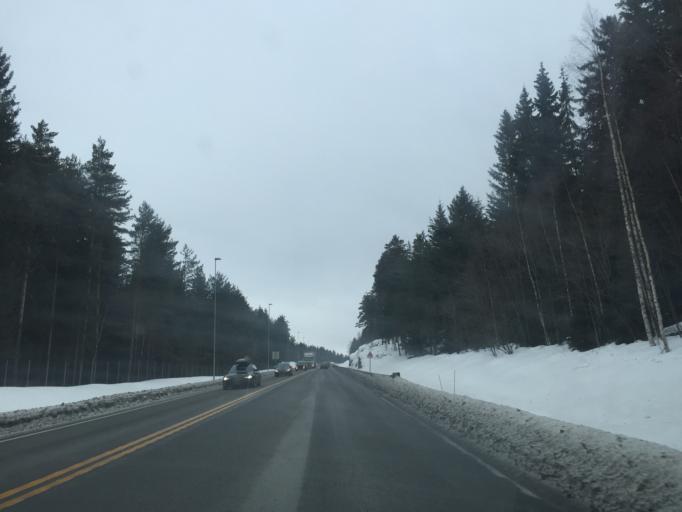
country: NO
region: Hedmark
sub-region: Loten
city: Loten
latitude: 60.7439
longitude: 11.3001
